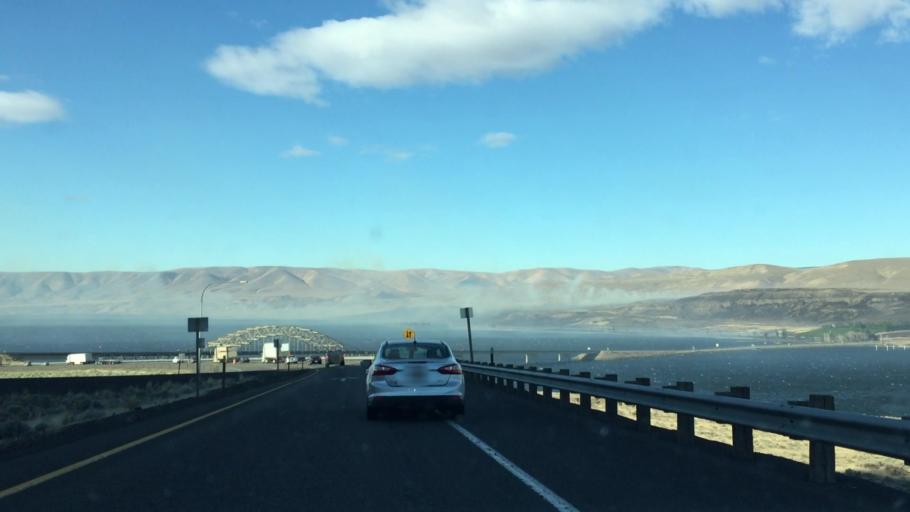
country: US
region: Washington
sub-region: Grant County
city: Mattawa
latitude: 46.9511
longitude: -119.9635
